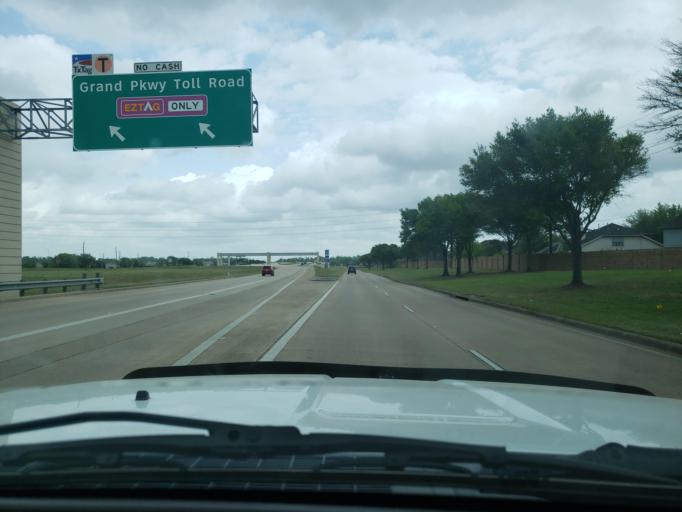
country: US
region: Texas
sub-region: Fort Bend County
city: Greatwood
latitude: 29.5695
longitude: -95.6843
